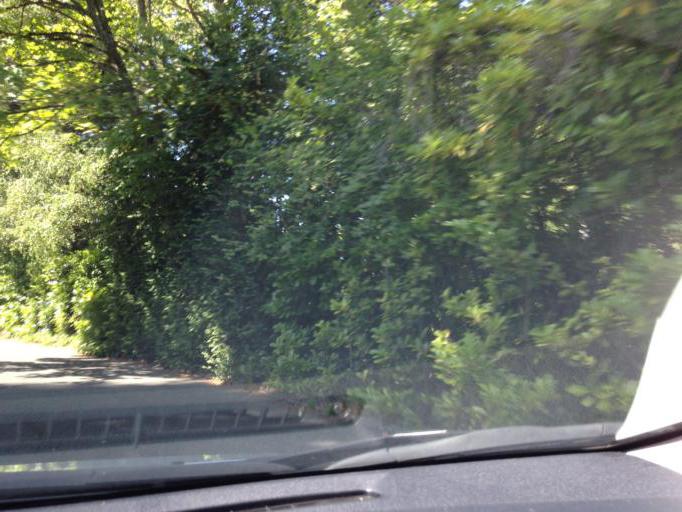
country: US
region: Washington
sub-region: King County
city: Seattle
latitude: 47.6206
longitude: -122.2820
